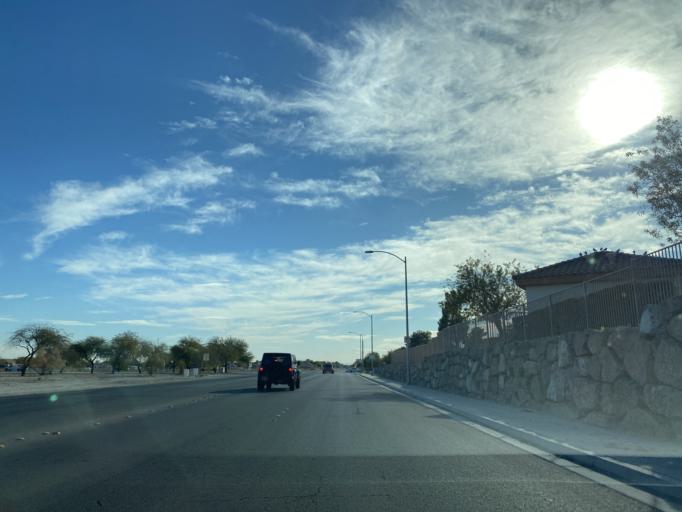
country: US
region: Nevada
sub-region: Clark County
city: North Las Vegas
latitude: 36.3068
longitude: -115.2422
